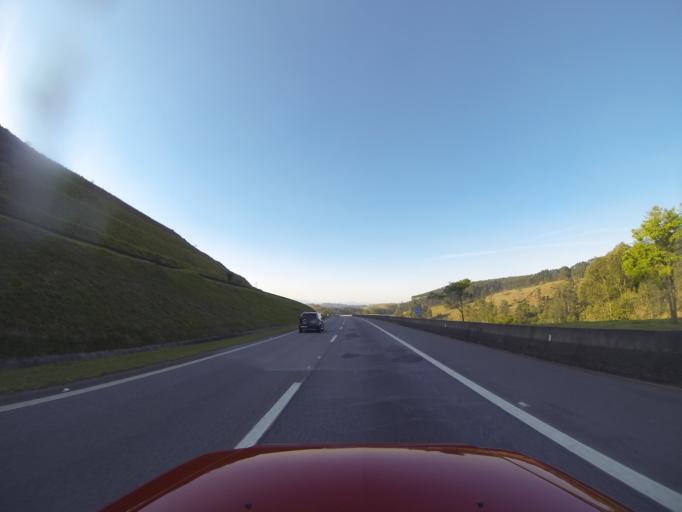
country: BR
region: Sao Paulo
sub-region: Jacarei
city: Jacarei
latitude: -23.2537
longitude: -46.0870
